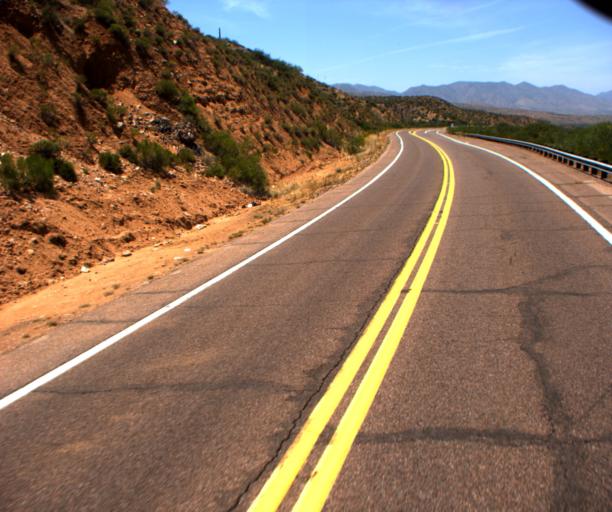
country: US
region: Arizona
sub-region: Gila County
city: Tonto Basin
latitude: 33.7412
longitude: -111.2235
